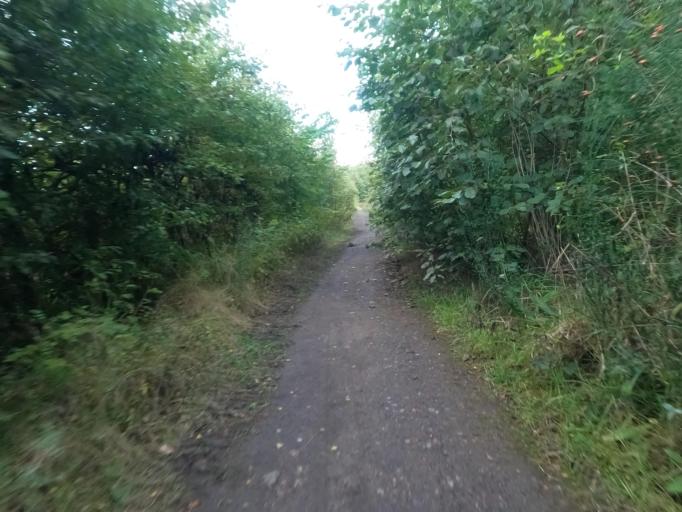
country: GB
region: England
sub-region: Northumberland
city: Seghill
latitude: 55.0701
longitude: -1.5471
